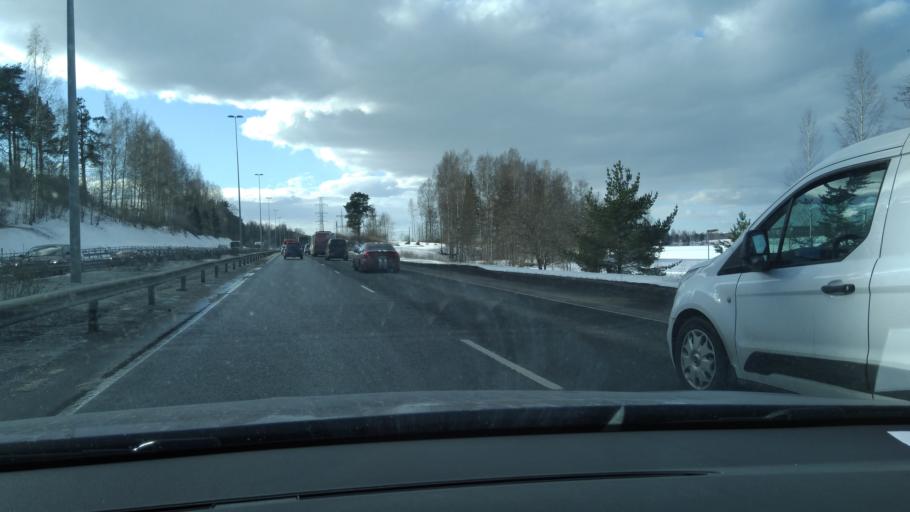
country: FI
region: Pirkanmaa
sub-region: Tampere
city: Tampere
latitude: 61.5072
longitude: 23.7080
